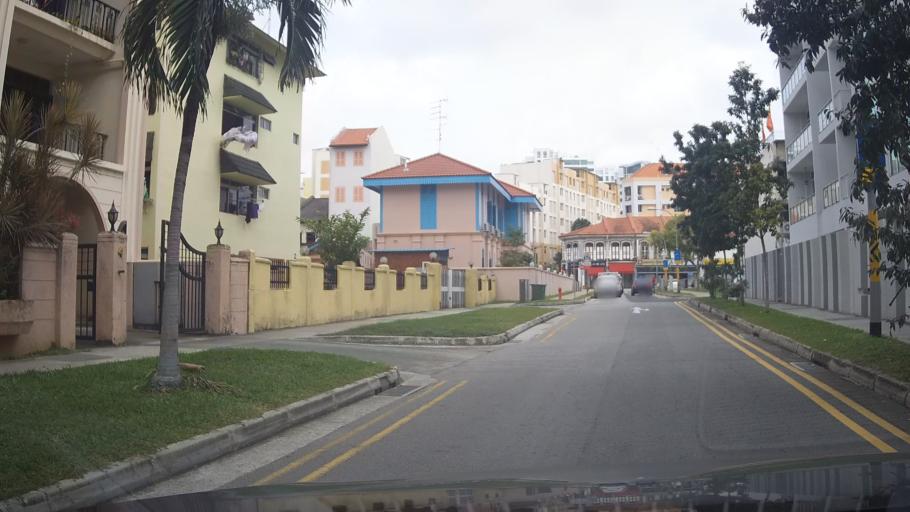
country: SG
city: Singapore
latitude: 1.3125
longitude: 103.8849
